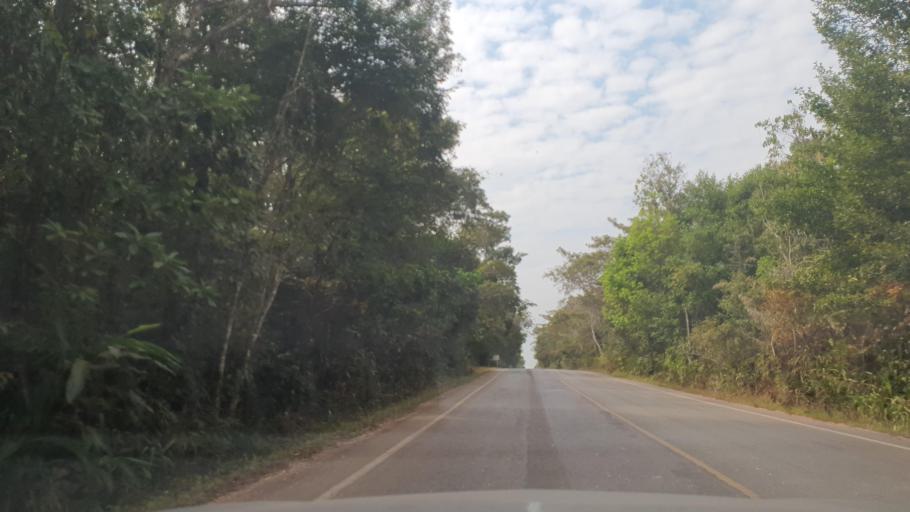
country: TH
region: Changwat Bueng Kan
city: Bung Khla
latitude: 18.2914
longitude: 103.9145
